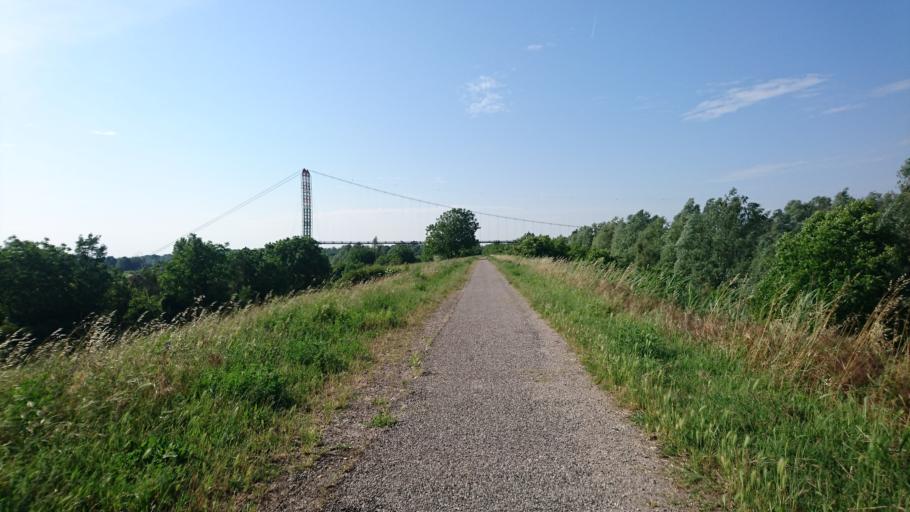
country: IT
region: Veneto
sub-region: Provincia di Verona
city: Villa Bartolomea
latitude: 45.1805
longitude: 11.3293
